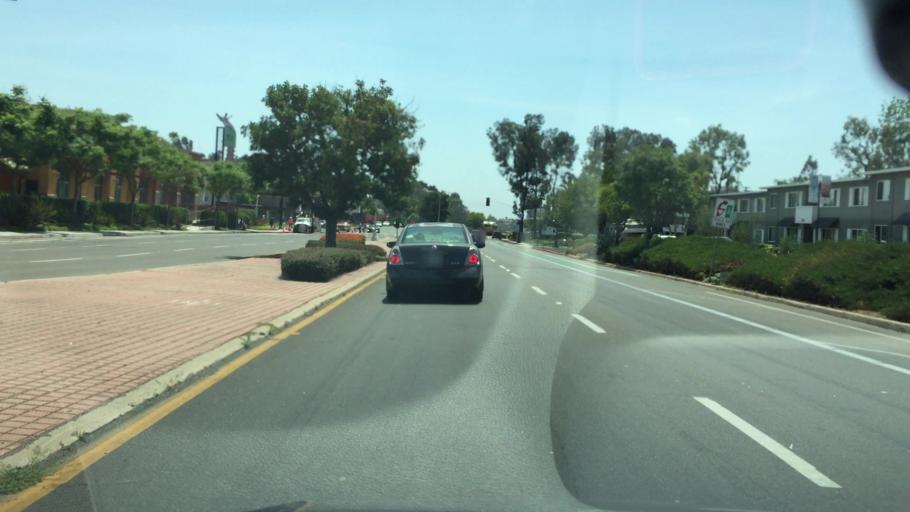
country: US
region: California
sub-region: San Diego County
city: Lemon Grove
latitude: 32.7498
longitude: -117.0716
